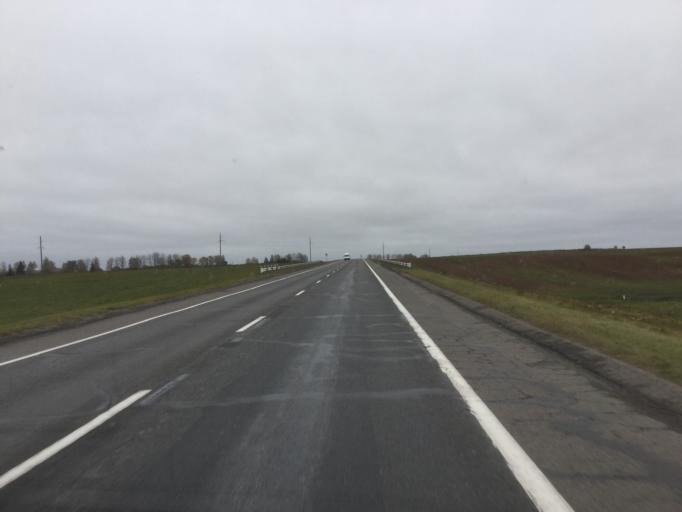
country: BY
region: Vitebsk
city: Chashniki
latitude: 55.0097
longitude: 29.1596
